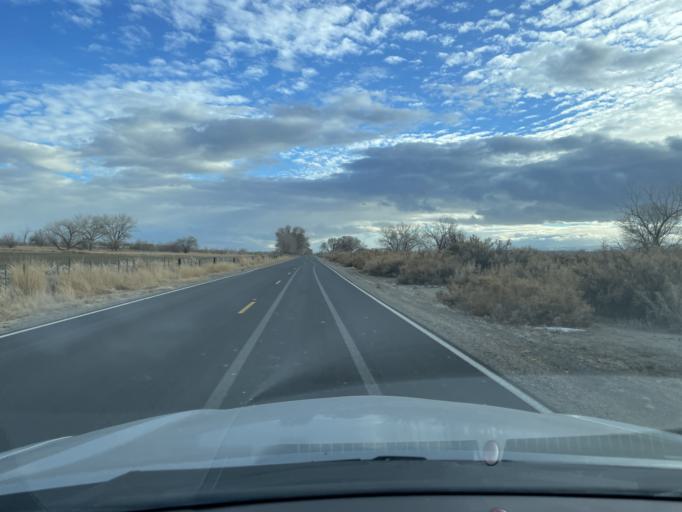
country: US
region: Colorado
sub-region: Montrose County
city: Olathe
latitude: 38.6394
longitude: -107.9922
